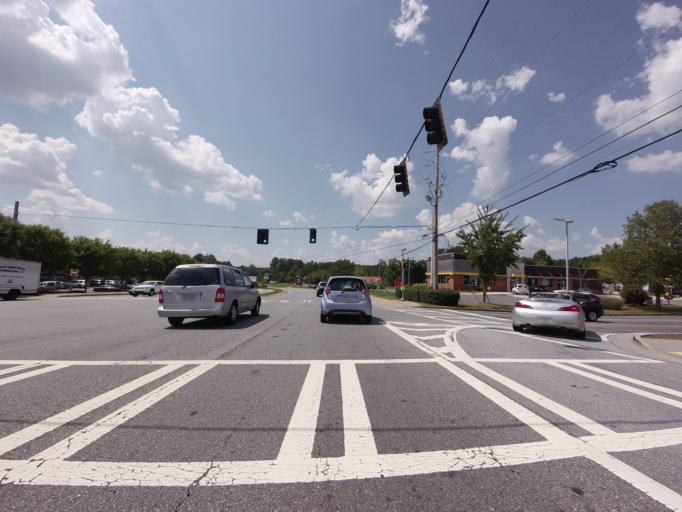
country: US
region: Georgia
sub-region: Fulton County
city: Johns Creek
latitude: 34.0488
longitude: -84.2245
